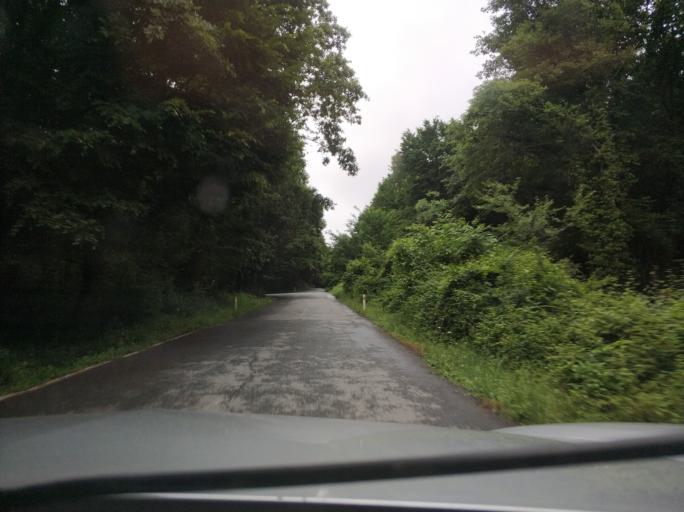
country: TR
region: Istanbul
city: Kemerburgaz
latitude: 41.1981
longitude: 28.9297
